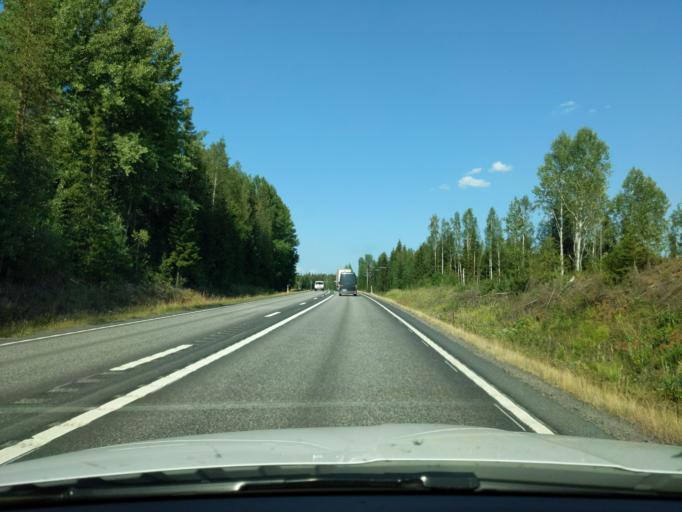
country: FI
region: Paijanne Tavastia
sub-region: Lahti
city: Jaervelae
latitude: 60.9133
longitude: 25.3492
